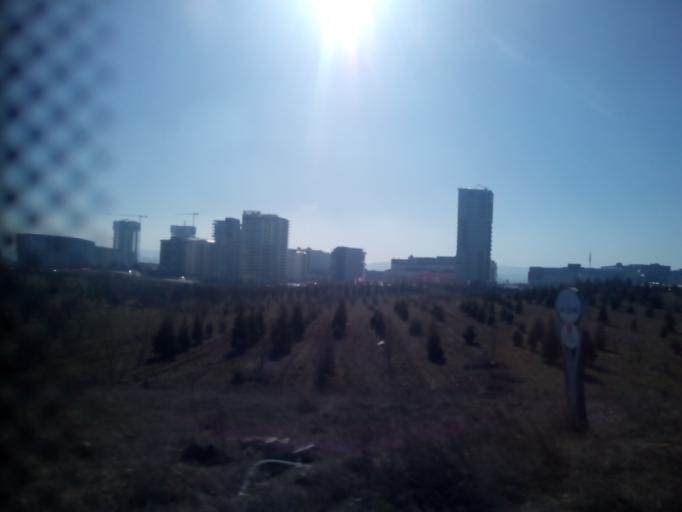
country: TR
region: Ankara
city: Batikent
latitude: 39.9167
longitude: 32.7771
